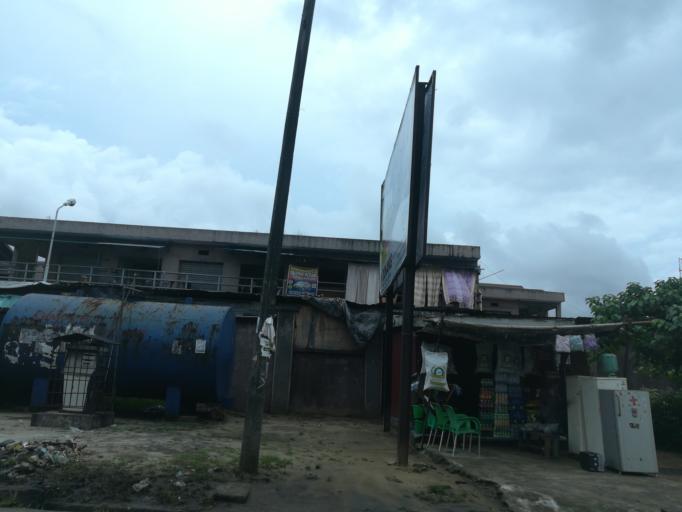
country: NG
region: Rivers
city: Port Harcourt
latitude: 4.7592
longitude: 7.0331
